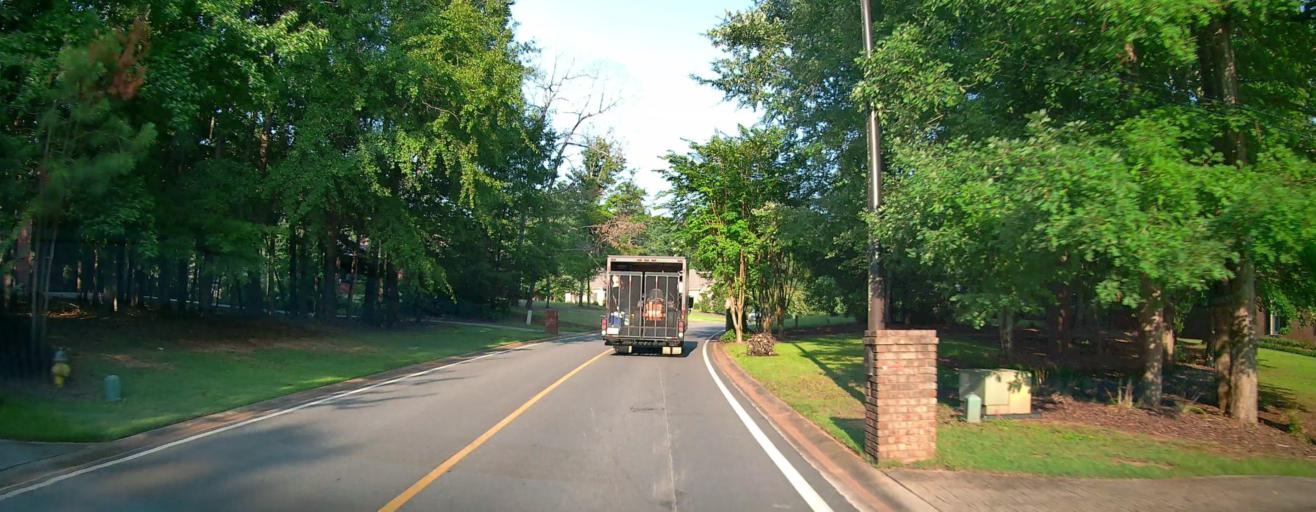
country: US
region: Georgia
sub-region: Bibb County
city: West Point
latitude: 32.8880
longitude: -83.8110
